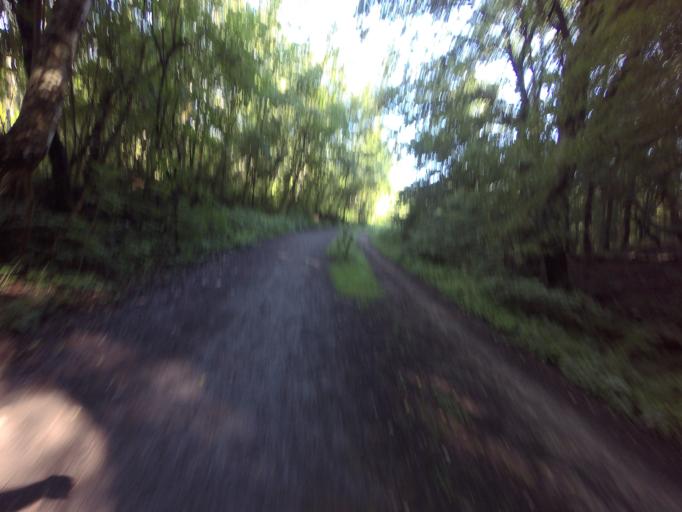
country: DE
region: North Rhine-Westphalia
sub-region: Regierungsbezirk Koln
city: Wurselen
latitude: 50.8264
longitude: 6.1117
